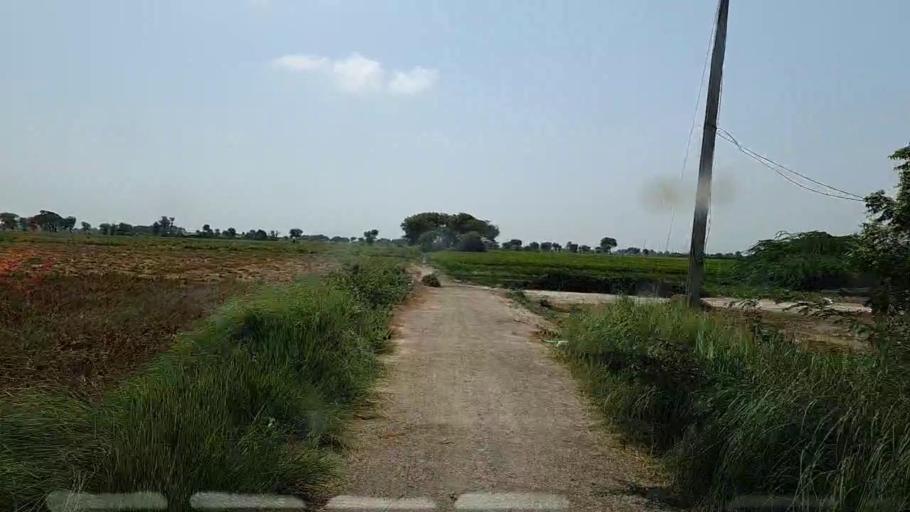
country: PK
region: Sindh
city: Kario
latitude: 24.6257
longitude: 68.5320
